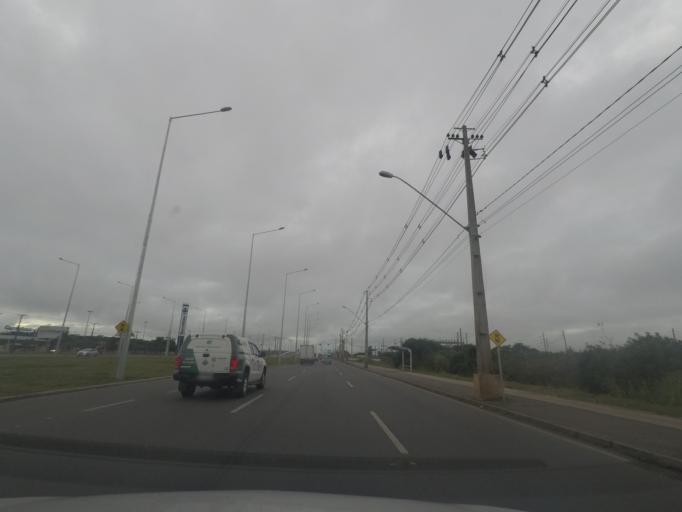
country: BR
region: Parana
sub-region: Pinhais
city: Pinhais
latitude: -25.4365
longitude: -49.1681
